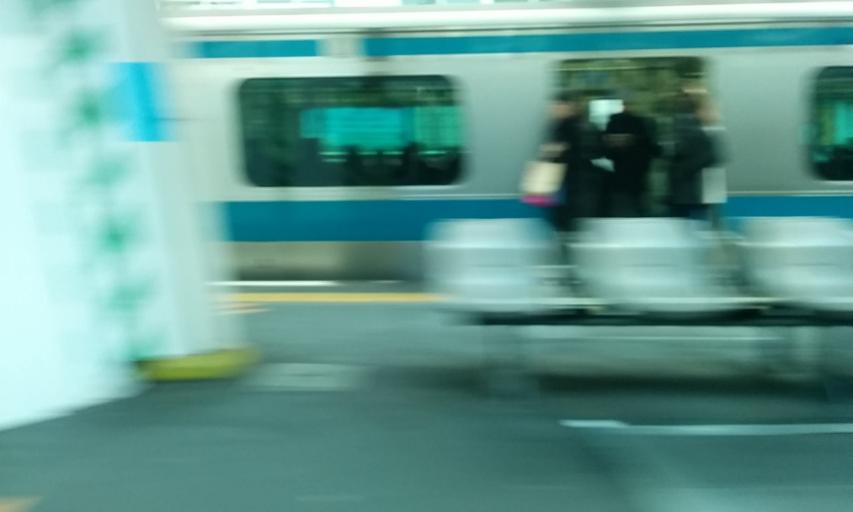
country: JP
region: Saitama
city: Kawaguchi
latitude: 35.8153
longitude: 139.7049
